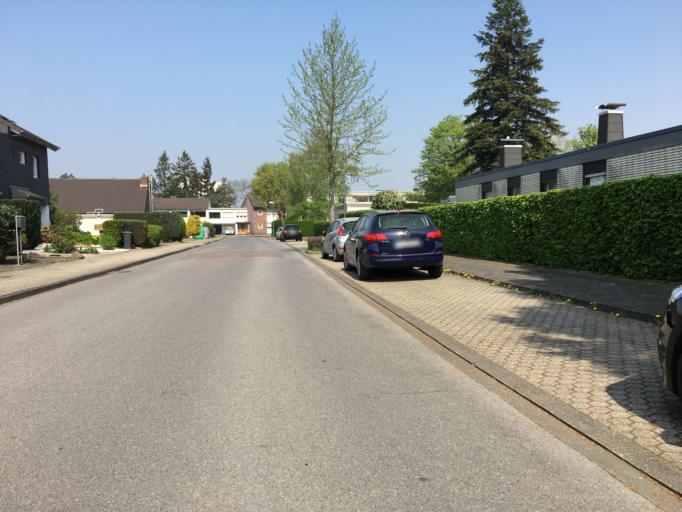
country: DE
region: North Rhine-Westphalia
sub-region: Regierungsbezirk Koln
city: Dueren
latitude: 50.7987
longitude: 6.4986
